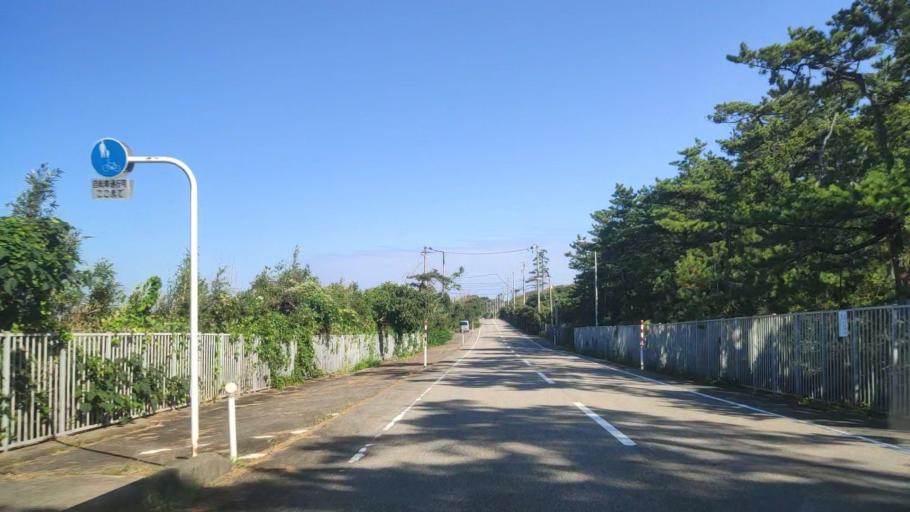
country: JP
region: Ishikawa
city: Hakui
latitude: 37.0631
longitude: 136.7231
